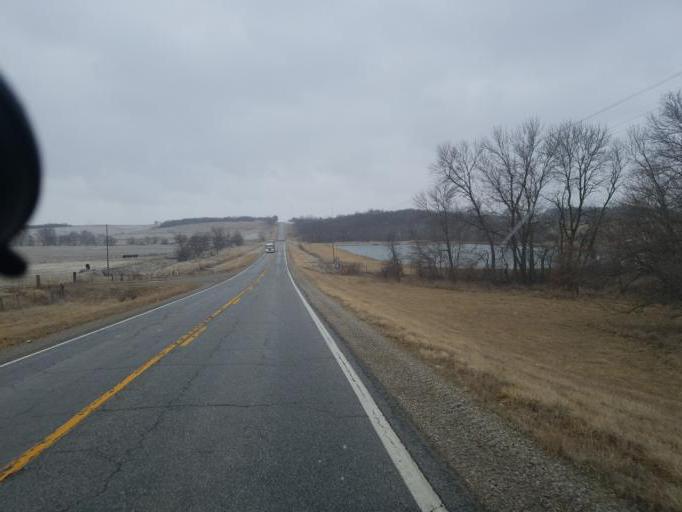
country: US
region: Missouri
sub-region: Putnam County
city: Unionville
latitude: 40.5336
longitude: -93.0181
